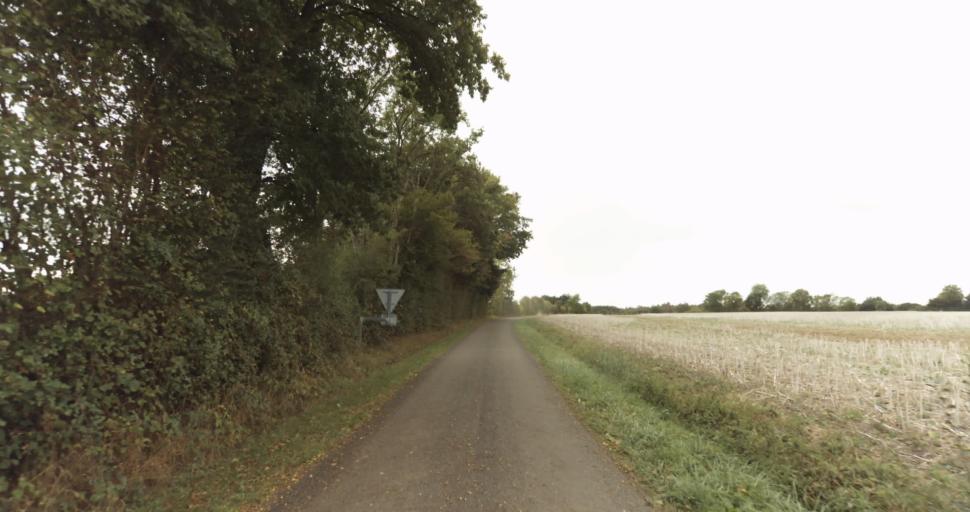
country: FR
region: Lower Normandy
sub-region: Departement de l'Orne
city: Sainte-Gauburge-Sainte-Colombe
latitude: 48.7285
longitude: 0.4315
